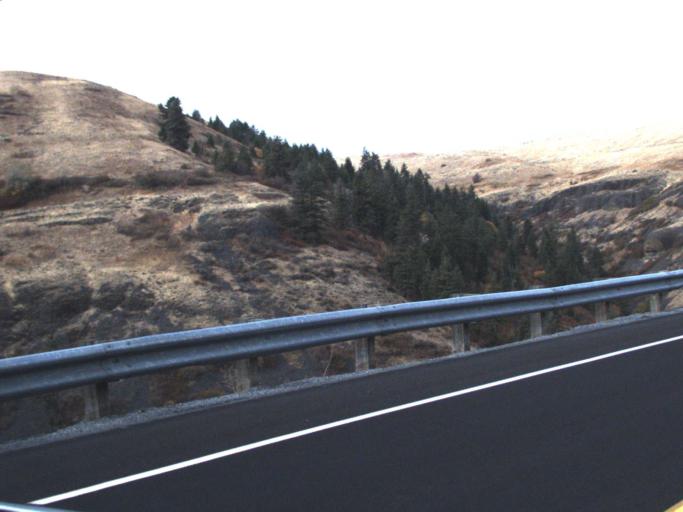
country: US
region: Washington
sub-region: Okanogan County
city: Coulee Dam
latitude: 47.8683
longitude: -118.7250
